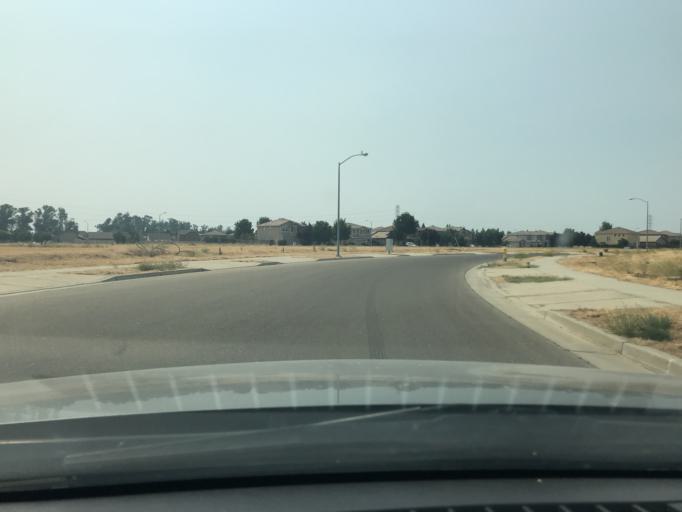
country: US
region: California
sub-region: Merced County
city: Merced
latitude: 37.3454
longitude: -120.4819
